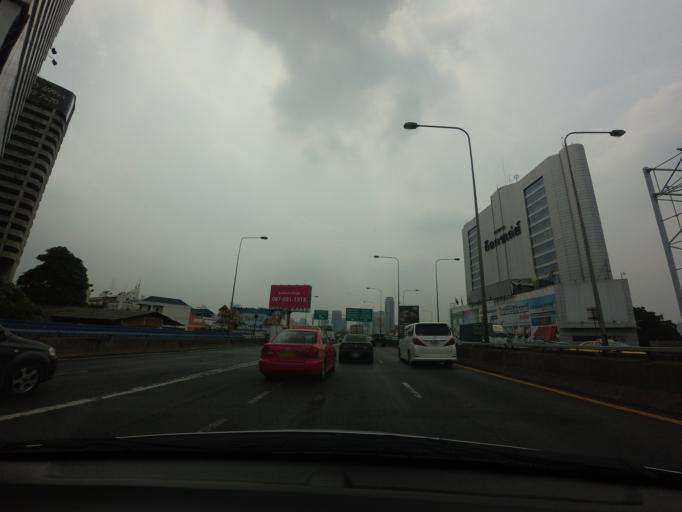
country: TH
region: Bangkok
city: Khlong Toei
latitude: 13.7150
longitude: 100.5583
